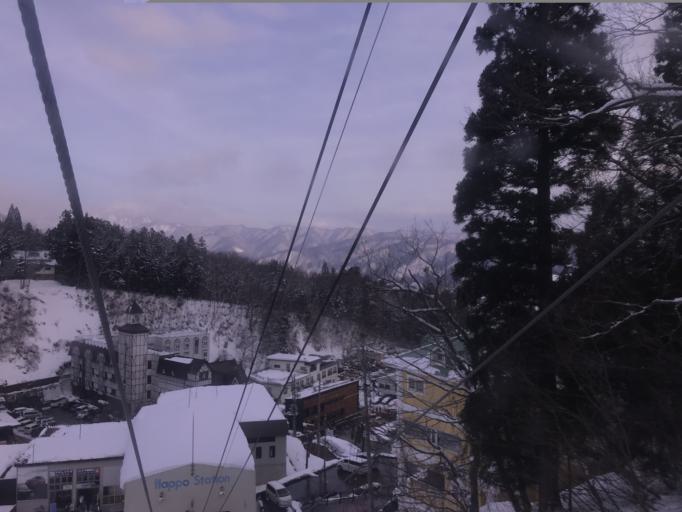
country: JP
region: Nagano
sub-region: Kitaazumi Gun
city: Hakuba
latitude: 36.7017
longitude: 137.8363
